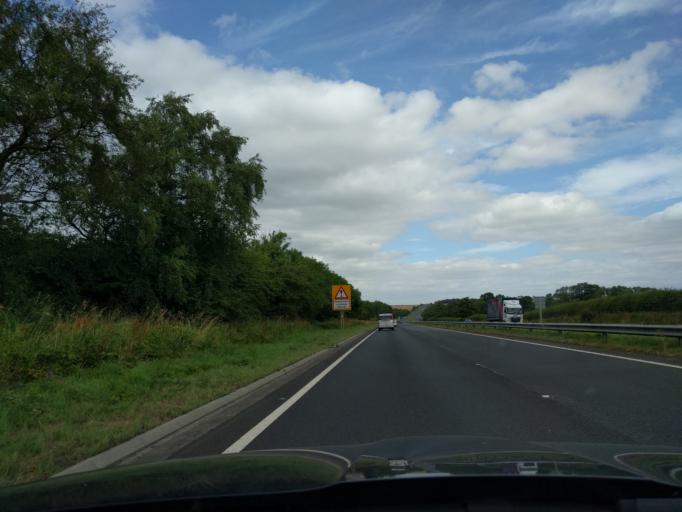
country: GB
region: England
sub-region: Northumberland
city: Felton
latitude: 55.3438
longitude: -1.7272
